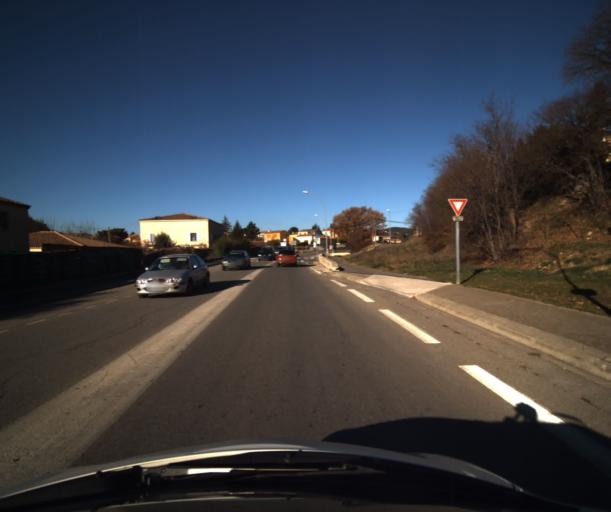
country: FR
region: Provence-Alpes-Cote d'Azur
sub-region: Departement du Vaucluse
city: Pertuis
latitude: 43.7006
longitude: 5.5000
